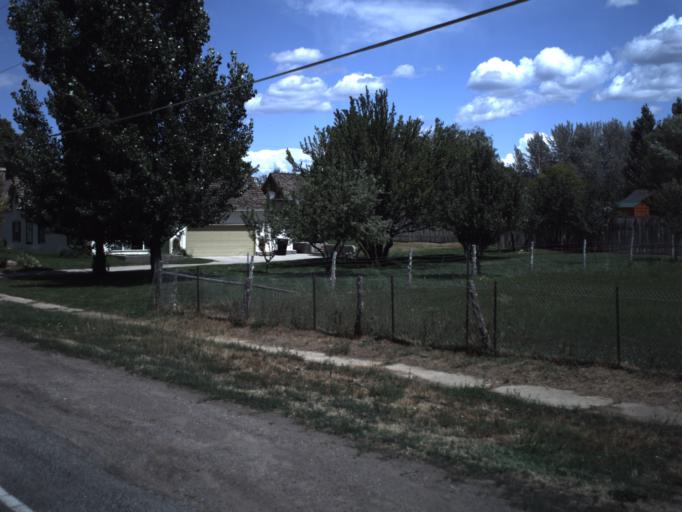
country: US
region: Utah
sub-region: Sanpete County
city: Mount Pleasant
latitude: 39.4829
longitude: -111.4961
